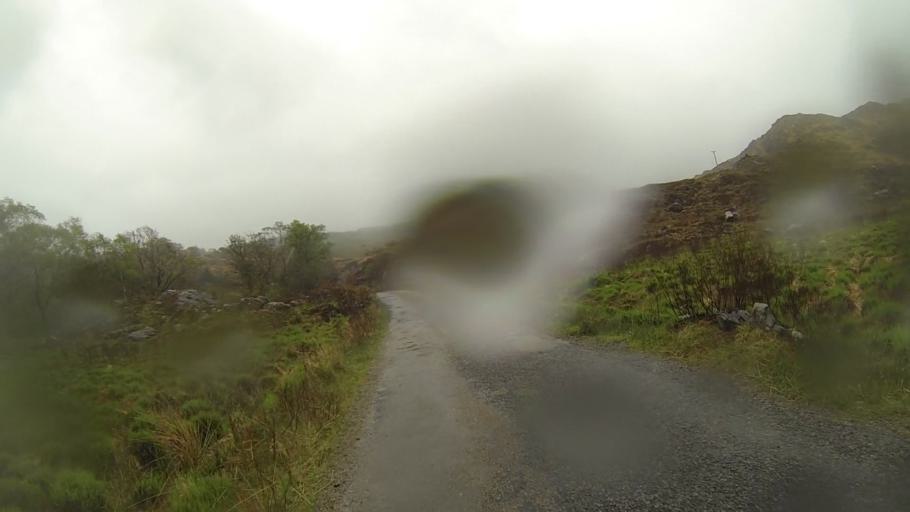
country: IE
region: Munster
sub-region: Ciarrai
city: Kenmare
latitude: 51.9613
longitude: -9.6359
